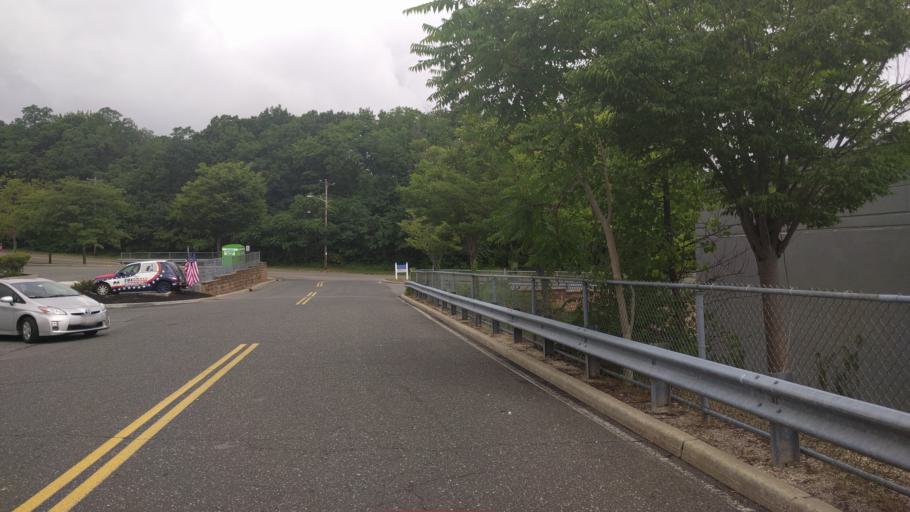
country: US
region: New York
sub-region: Suffolk County
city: Huntington Station
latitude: 40.8582
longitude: -73.4201
